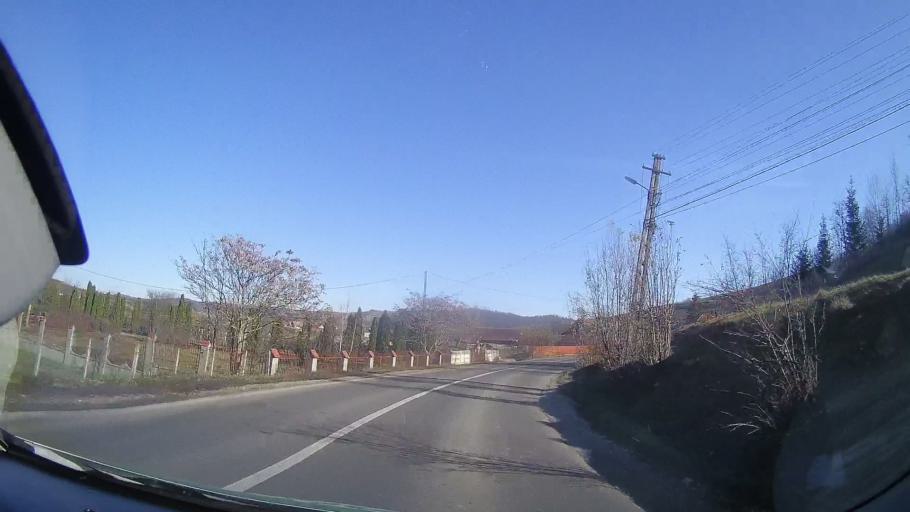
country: RO
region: Mures
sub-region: Comuna Sarmasu
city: Sarmasu
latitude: 46.7638
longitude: 24.1825
